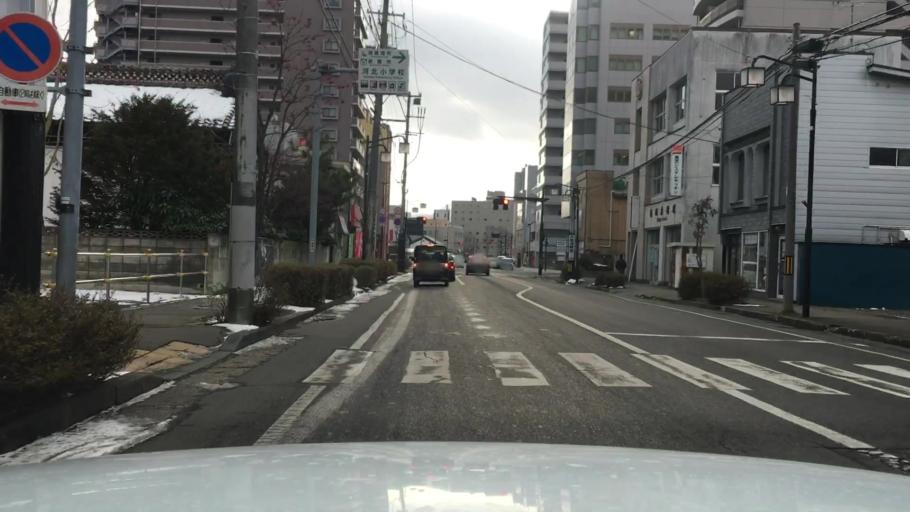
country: JP
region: Iwate
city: Morioka-shi
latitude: 39.7071
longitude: 141.1408
